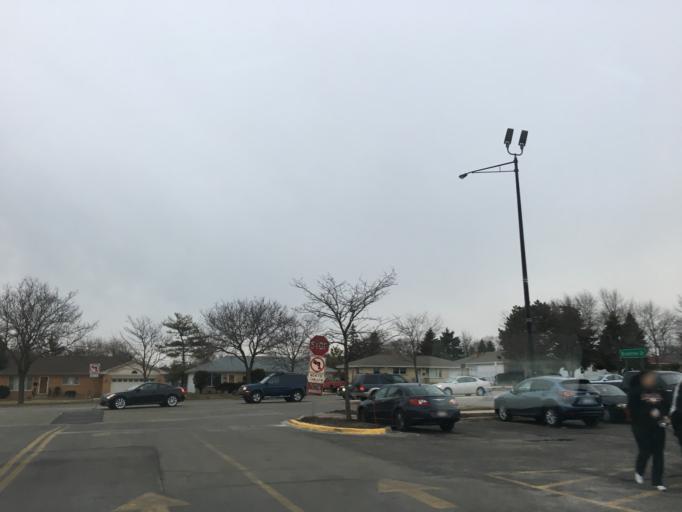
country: US
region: Illinois
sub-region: Cook County
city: Schaumburg
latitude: 42.0267
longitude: -88.1080
